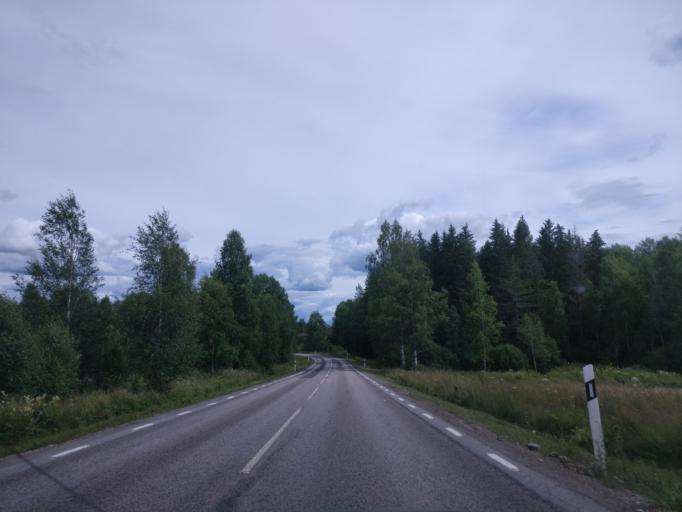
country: SE
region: Vaermland
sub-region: Hagfors Kommun
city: Ekshaerad
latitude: 60.1528
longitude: 13.4332
